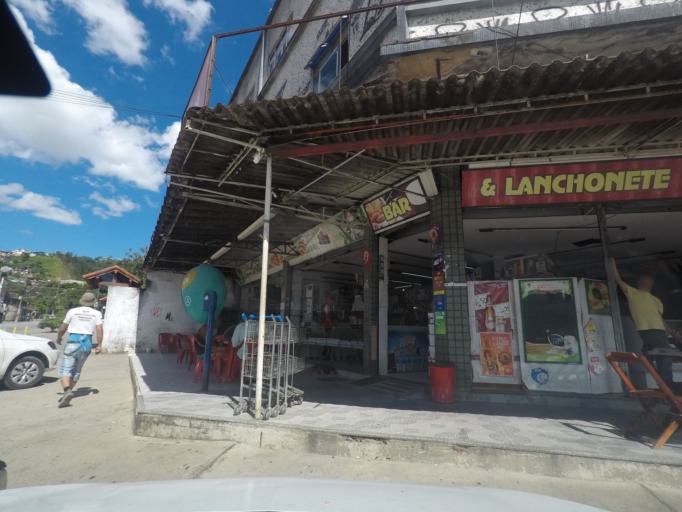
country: BR
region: Rio de Janeiro
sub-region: Teresopolis
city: Teresopolis
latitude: -22.4343
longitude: -42.9719
